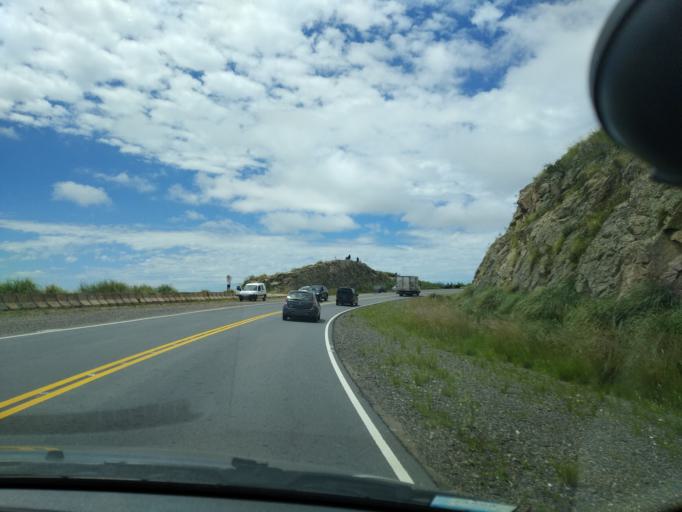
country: AR
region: Cordoba
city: Cuesta Blanca
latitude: -31.6018
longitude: -64.6960
